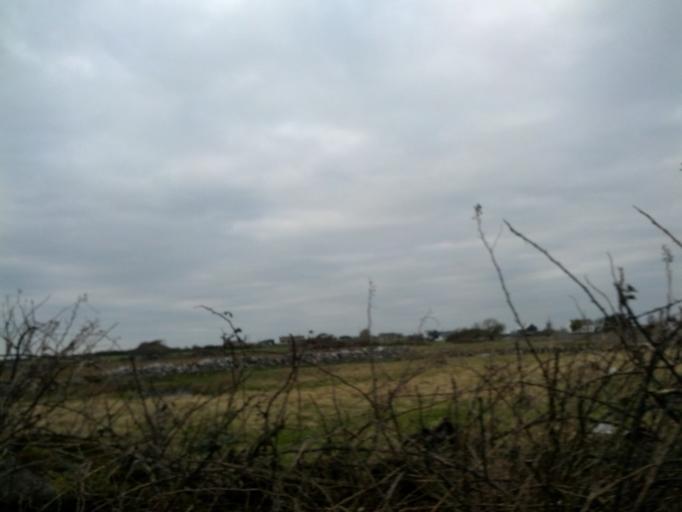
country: IE
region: Connaught
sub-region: County Galway
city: Oranmore
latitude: 53.1943
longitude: -8.9312
